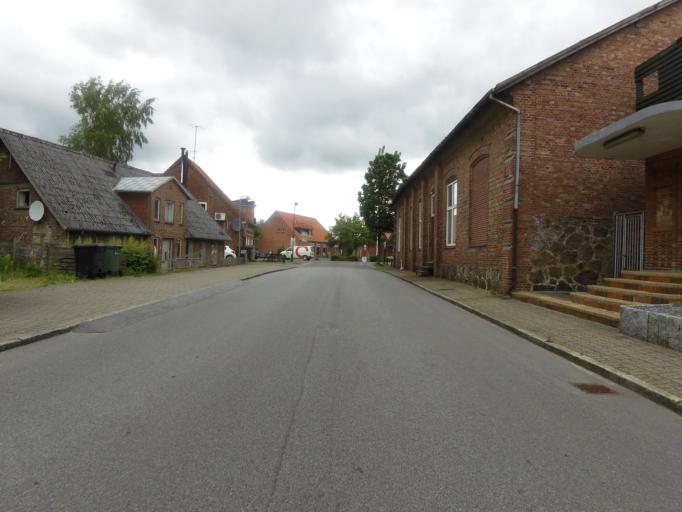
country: DK
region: South Denmark
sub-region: Haderslev Kommune
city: Gram
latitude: 55.2872
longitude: 9.0491
